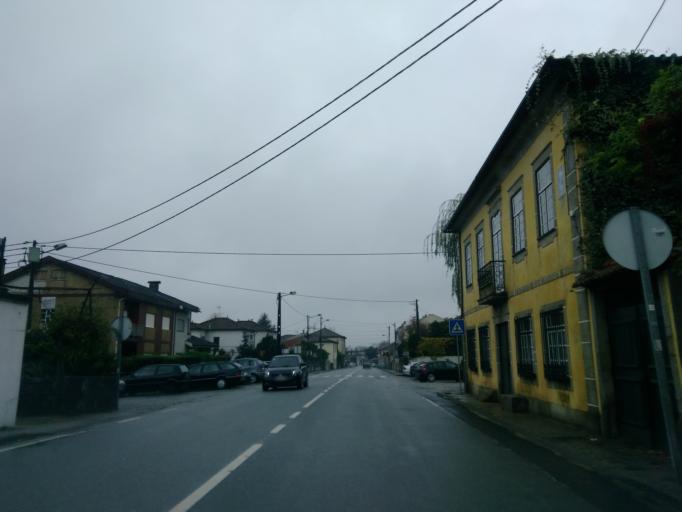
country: PT
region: Braga
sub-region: Braga
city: Adaufe
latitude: 41.5615
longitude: -8.3893
